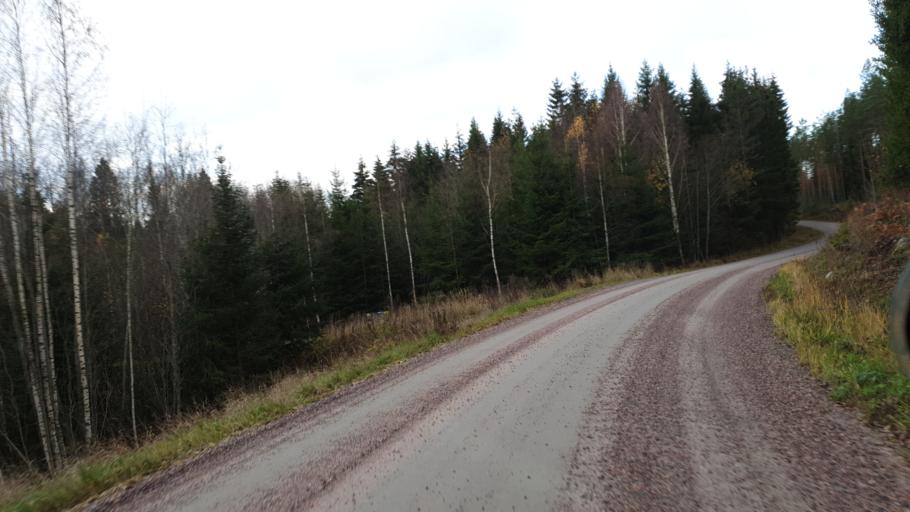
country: FI
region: Uusimaa
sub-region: Helsinki
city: Siuntio
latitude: 60.1553
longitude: 24.2834
